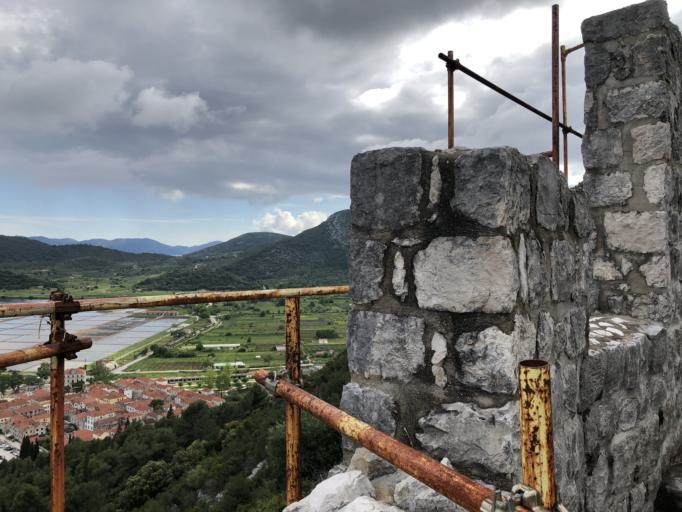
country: HR
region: Dubrovacko-Neretvanska
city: Ston
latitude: 42.8419
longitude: 17.6986
